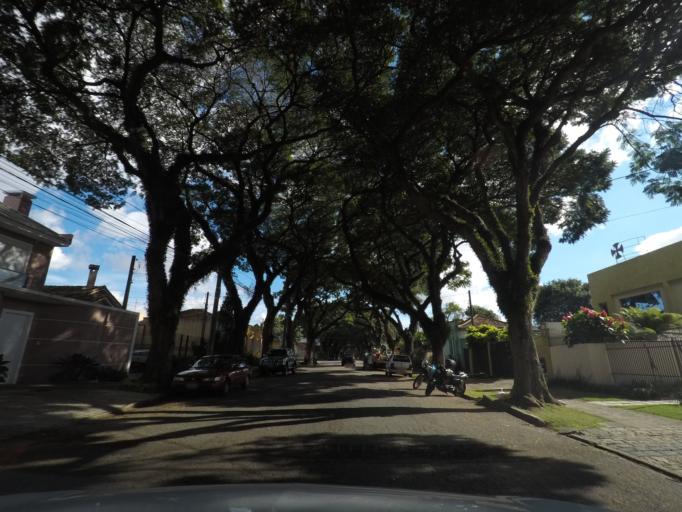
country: BR
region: Parana
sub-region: Curitiba
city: Curitiba
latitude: -25.4437
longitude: -49.2541
